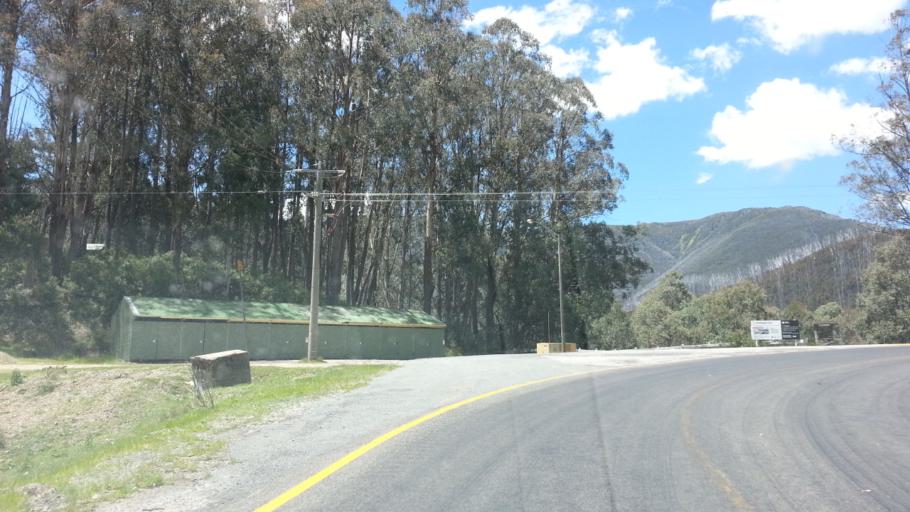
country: AU
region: Victoria
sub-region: Alpine
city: Mount Beauty
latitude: -36.8423
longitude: 147.2515
